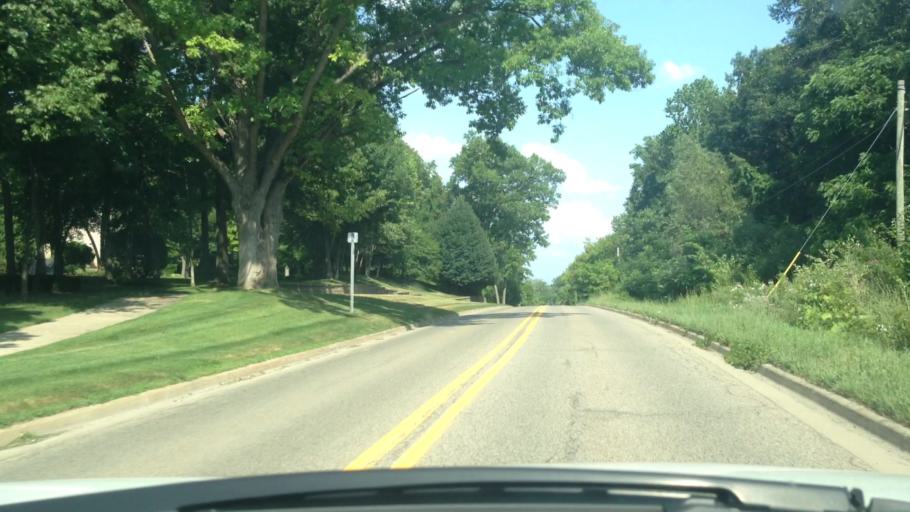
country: US
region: Michigan
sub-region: Oakland County
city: Clarkston
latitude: 42.7339
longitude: -83.3712
